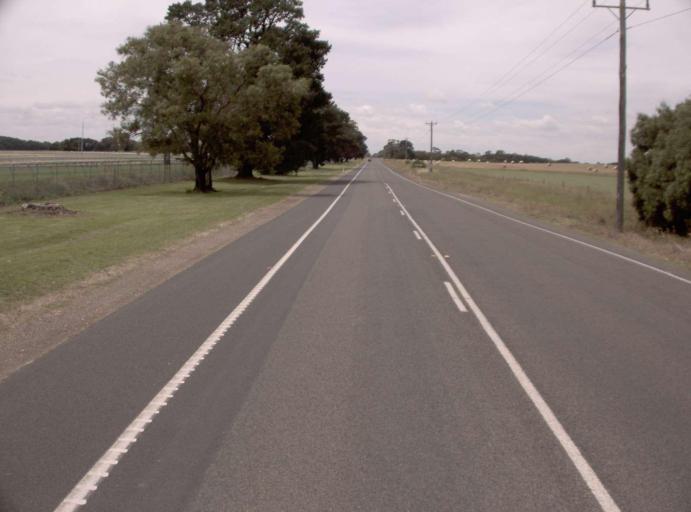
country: AU
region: Victoria
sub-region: Wellington
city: Sale
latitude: -38.0719
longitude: 147.0391
